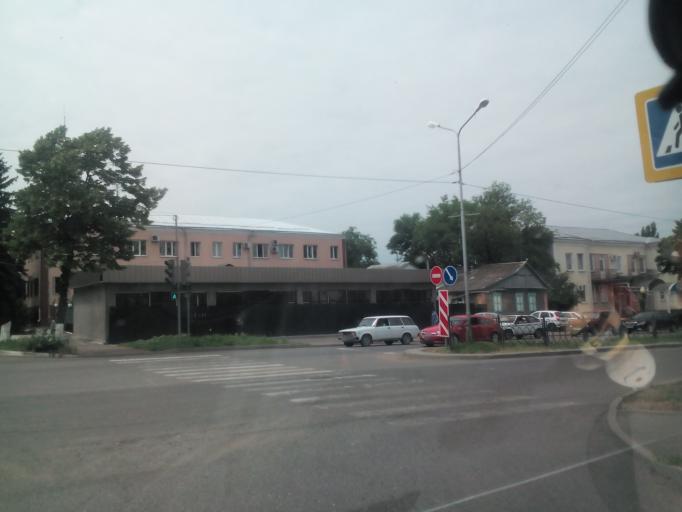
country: RU
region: Stavropol'skiy
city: Zheleznovodsk
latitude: 44.1445
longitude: 43.0023
